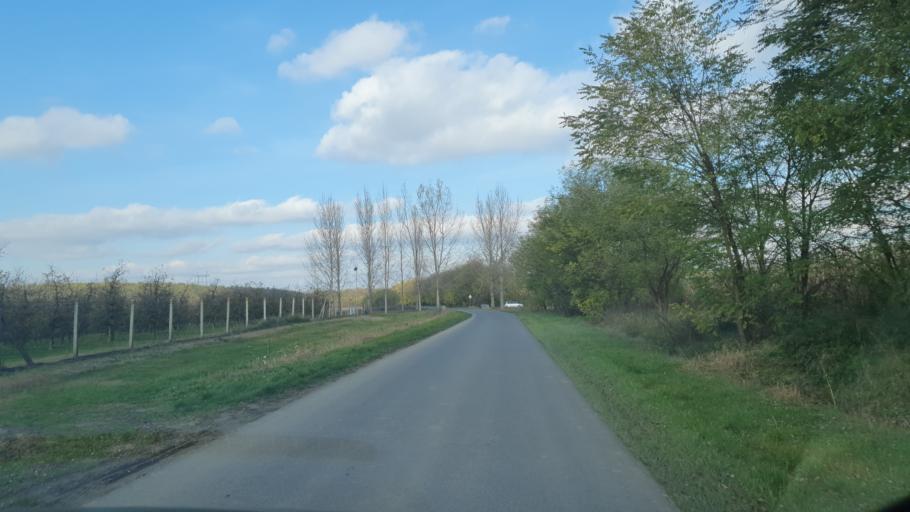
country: HU
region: Szabolcs-Szatmar-Bereg
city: Petnehaza
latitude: 48.0661
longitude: 22.0463
